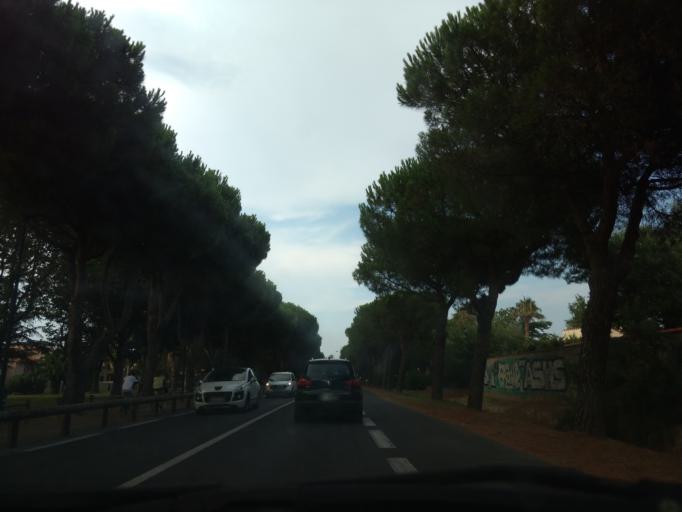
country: FR
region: Languedoc-Roussillon
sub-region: Departement des Pyrenees-Orientales
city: Saint-Cyprien-Plage
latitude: 42.6272
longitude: 3.0256
